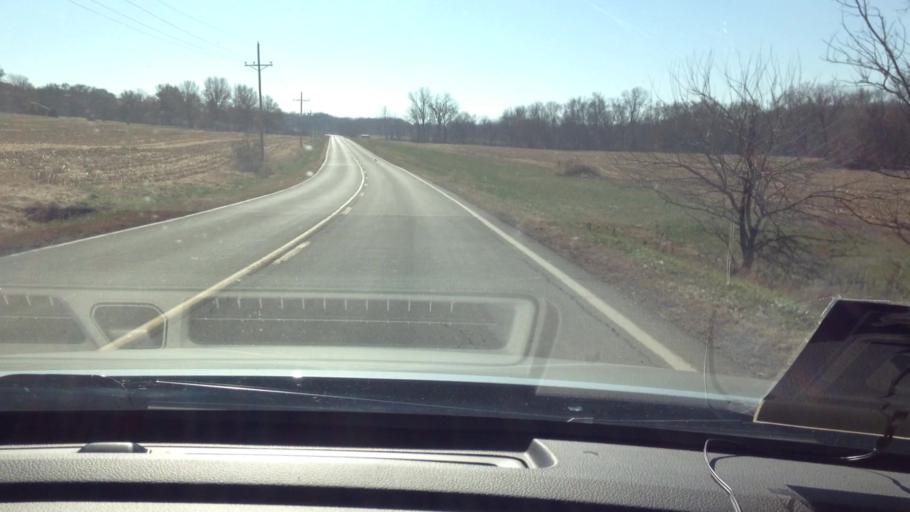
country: US
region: Missouri
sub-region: Platte County
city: Platte City
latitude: 39.4793
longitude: -94.8100
